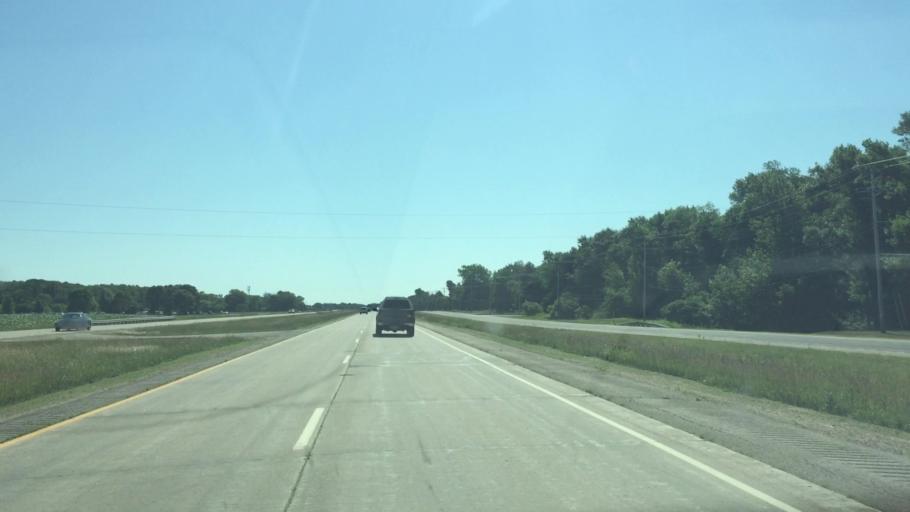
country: US
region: Wisconsin
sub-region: Outagamie County
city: Kimberly
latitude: 44.2075
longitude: -88.3567
